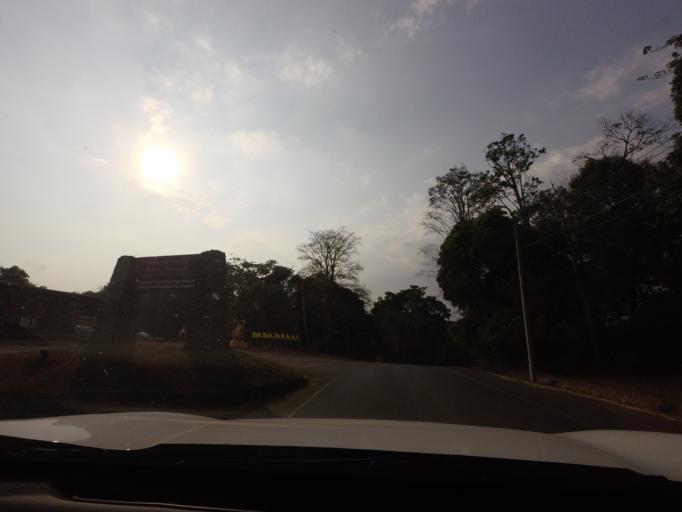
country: TH
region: Nakhon Nayok
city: Nakhon Nayok
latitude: 14.4113
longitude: 101.3731
